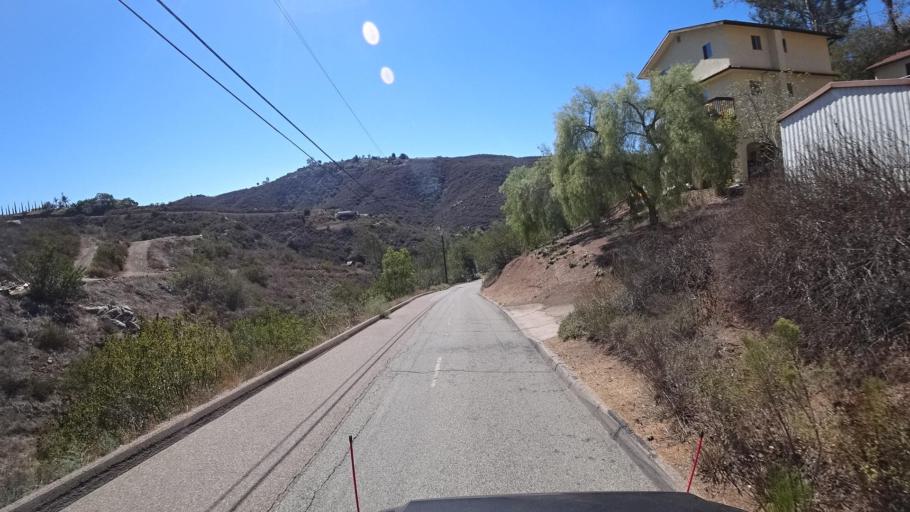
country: US
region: California
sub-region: San Diego County
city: Jamul
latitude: 32.7367
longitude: -116.8816
